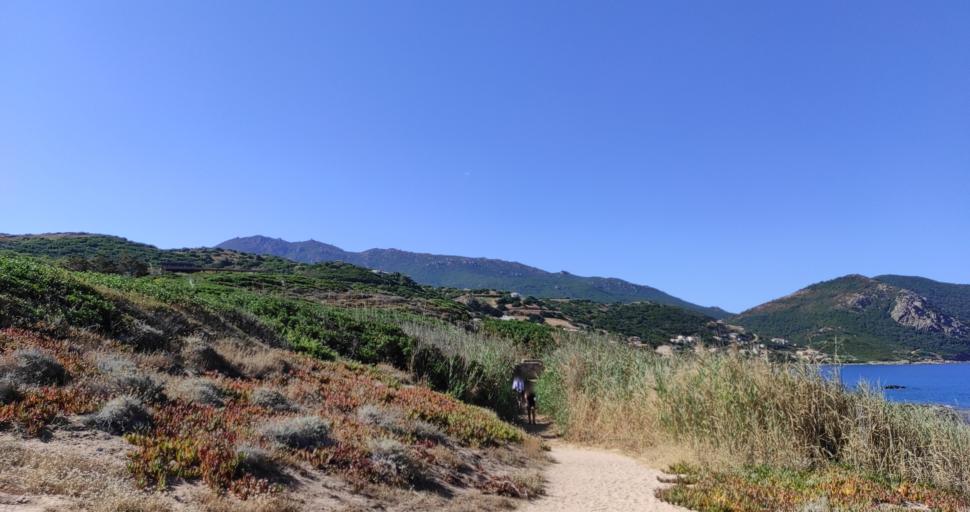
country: FR
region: Corsica
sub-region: Departement de la Corse-du-Sud
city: Alata
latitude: 41.9857
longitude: 8.6701
